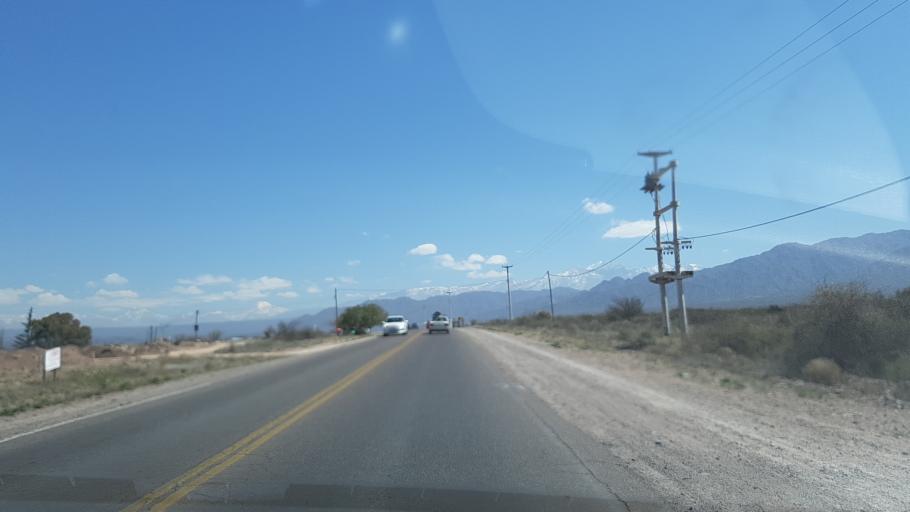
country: AR
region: Mendoza
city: Lujan de Cuyo
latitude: -33.0182
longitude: -68.9429
